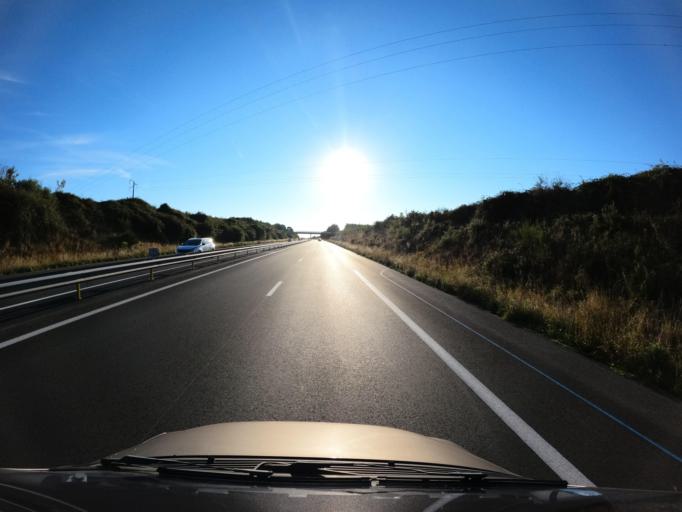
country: FR
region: Pays de la Loire
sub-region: Departement de la Vendee
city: La Gaubretiere
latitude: 46.9266
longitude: -1.0222
